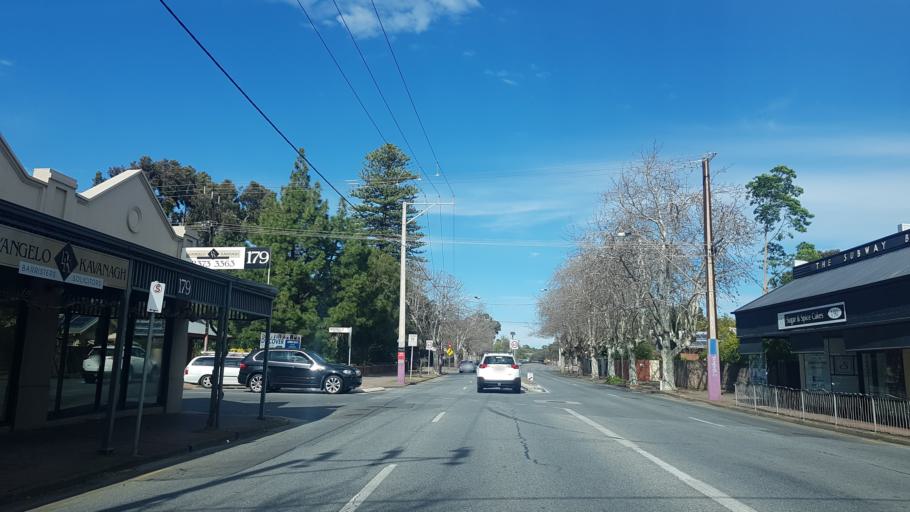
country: AU
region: South Australia
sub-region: Unley
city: Millswood
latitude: -34.9554
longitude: 138.5900
